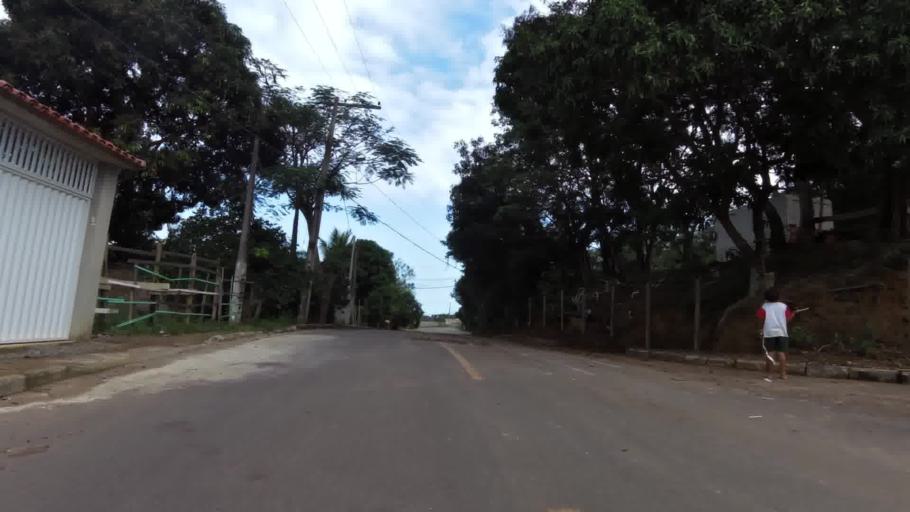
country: BR
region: Espirito Santo
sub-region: Piuma
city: Piuma
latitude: -20.7950
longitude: -40.6403
